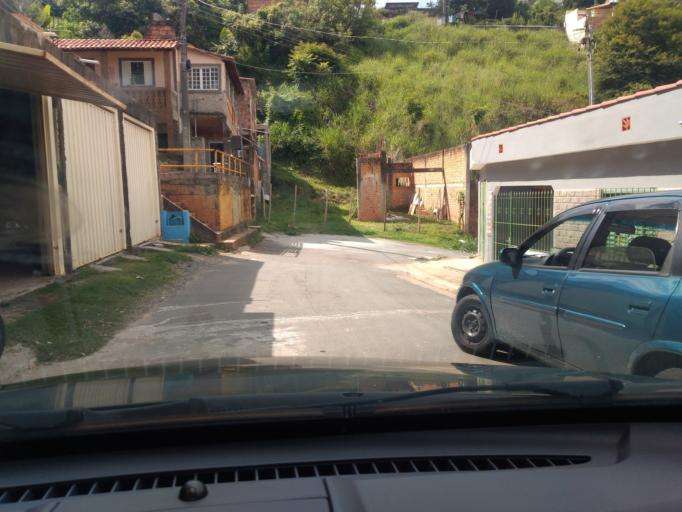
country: BR
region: Minas Gerais
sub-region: Tres Coracoes
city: Tres Coracoes
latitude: -21.6953
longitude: -45.2492
